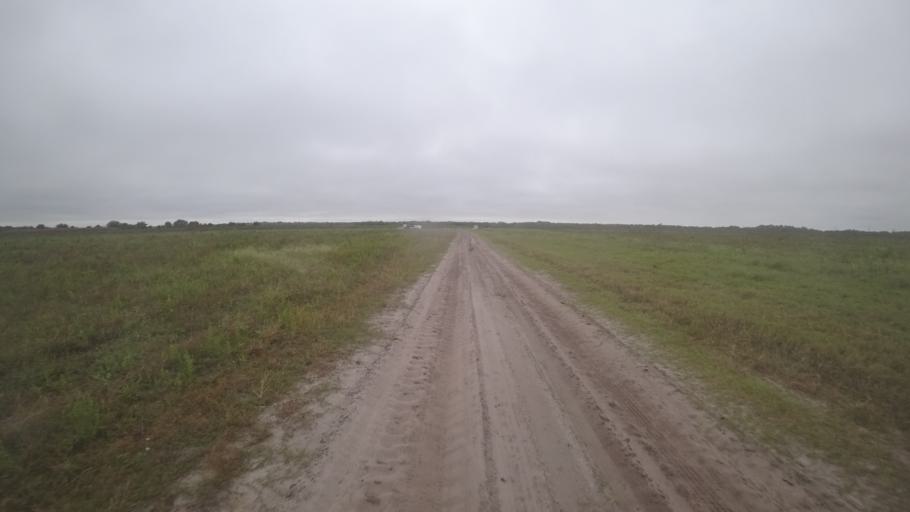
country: US
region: Florida
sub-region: Sarasota County
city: The Meadows
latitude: 27.4429
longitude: -82.3402
